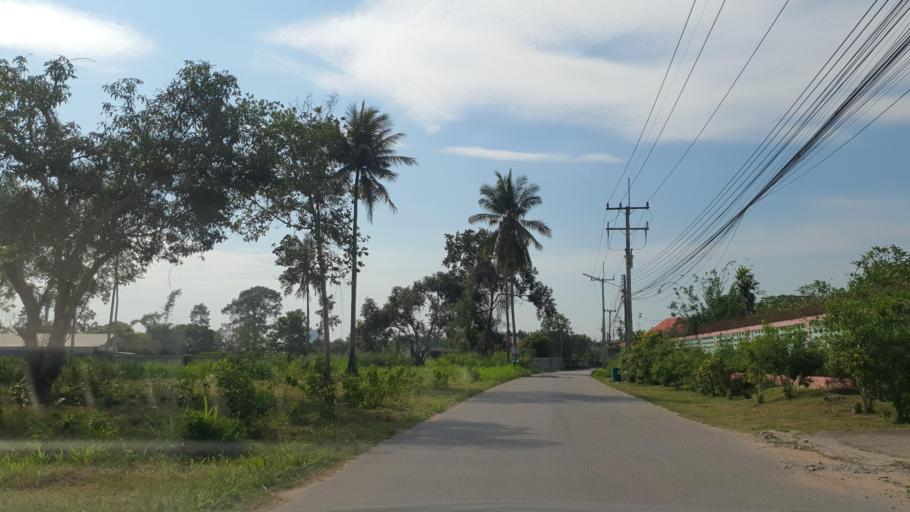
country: TH
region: Chon Buri
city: Sattahip
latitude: 12.7937
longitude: 100.9375
